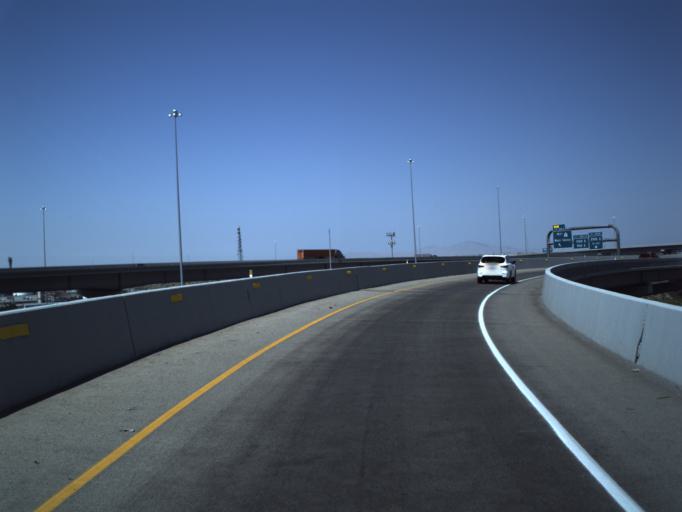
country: US
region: Utah
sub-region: Salt Lake County
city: South Salt Lake
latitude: 40.7191
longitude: -111.9022
